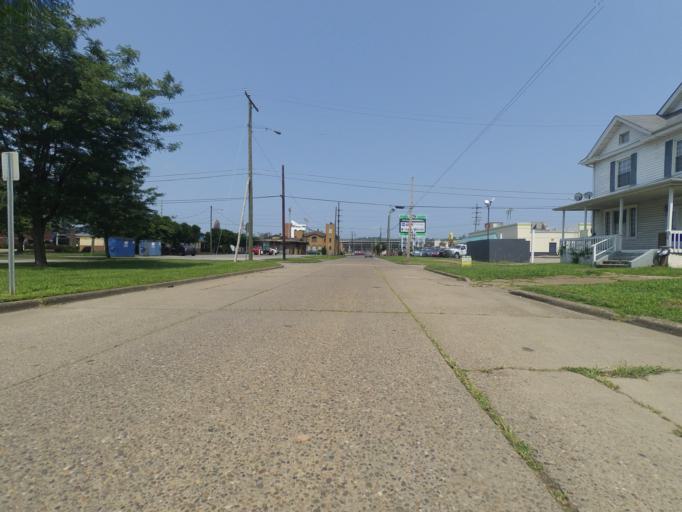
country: US
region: West Virginia
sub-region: Cabell County
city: Huntington
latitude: 38.4224
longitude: -82.4206
